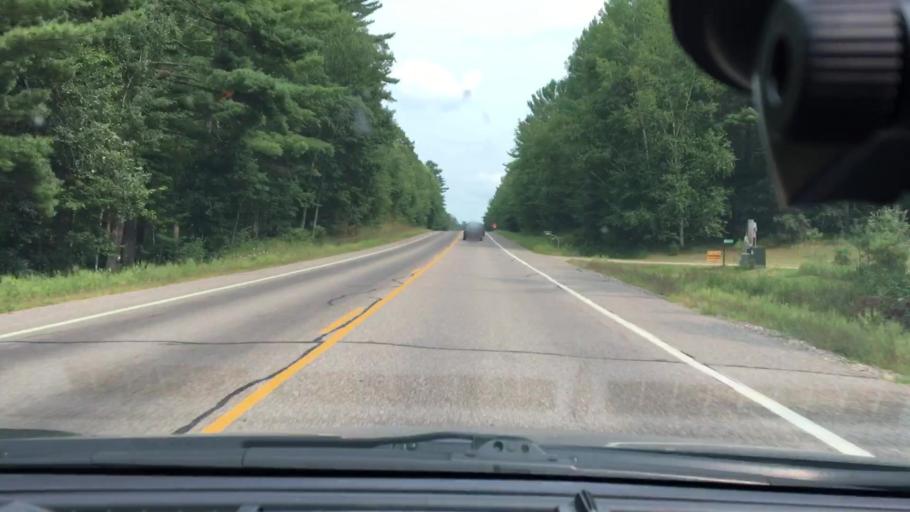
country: US
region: Minnesota
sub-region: Crow Wing County
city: Cross Lake
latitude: 46.7308
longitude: -93.9727
